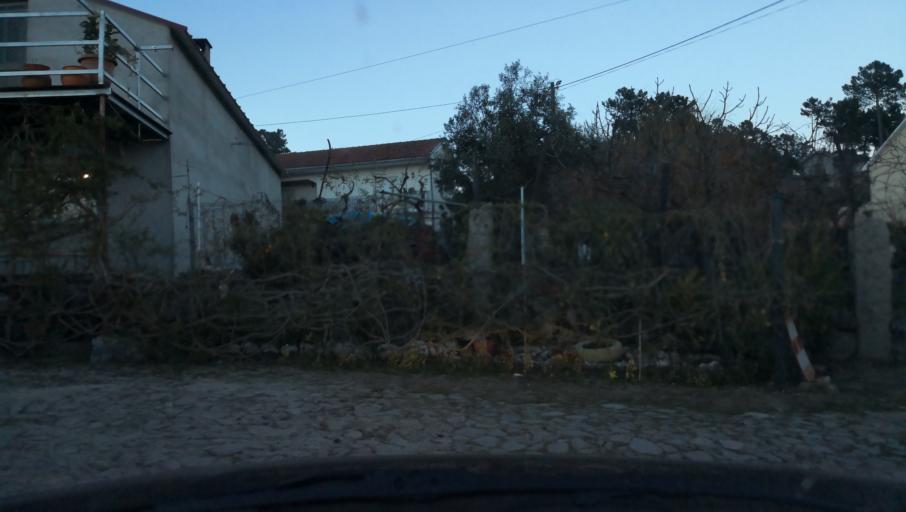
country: PT
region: Vila Real
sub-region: Vila Real
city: Vila Real
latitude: 41.3040
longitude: -7.7833
